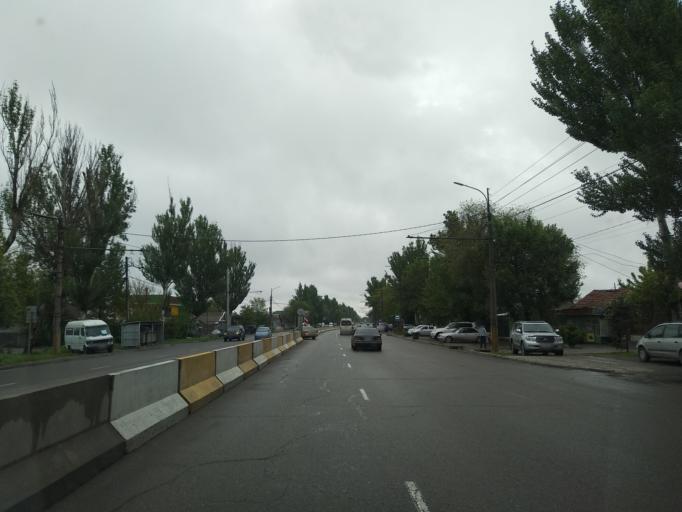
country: KG
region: Chuy
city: Lebedinovka
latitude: 42.8886
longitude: 74.6431
